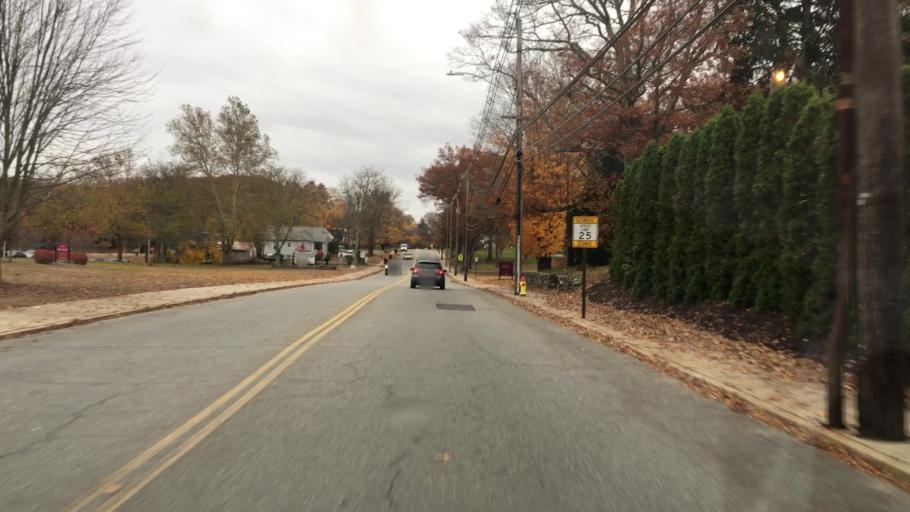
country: US
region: Connecticut
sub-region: Windham County
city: Willimantic
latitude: 41.7240
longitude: -72.2161
